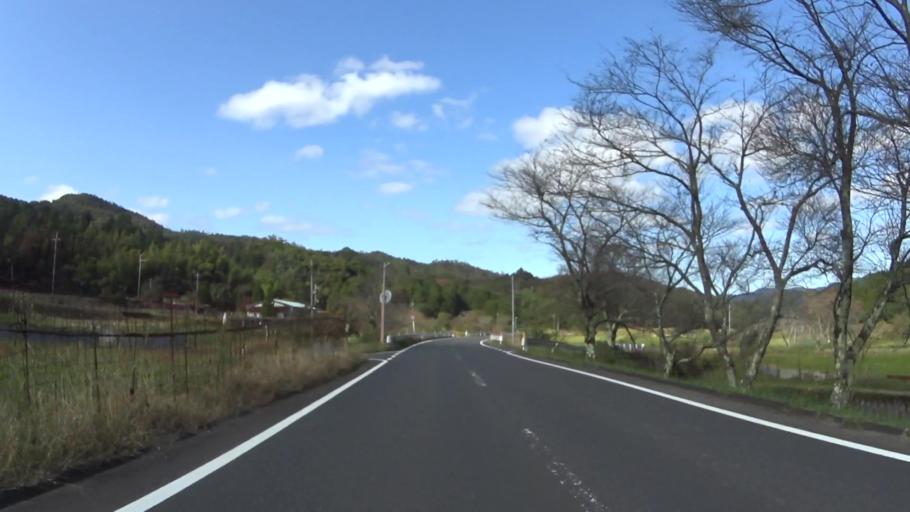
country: JP
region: Hyogo
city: Toyooka
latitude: 35.5485
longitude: 134.9780
